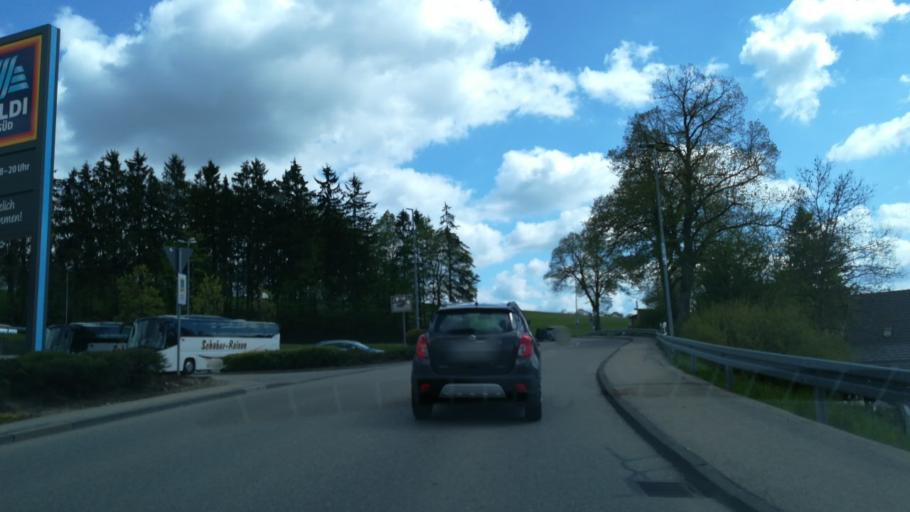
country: DE
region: Baden-Wuerttemberg
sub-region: Freiburg Region
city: Bonndorf im Schwarzwald
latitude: 47.8190
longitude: 8.3466
